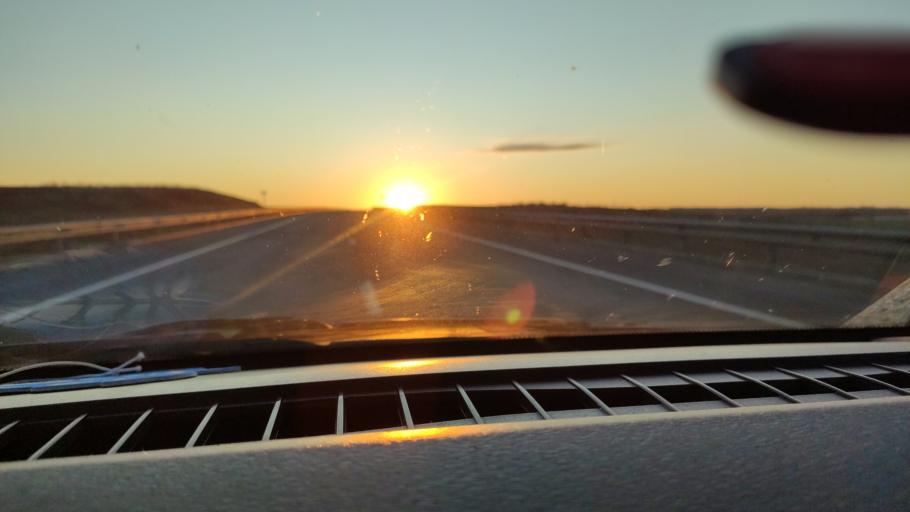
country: RU
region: Saratov
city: Yelshanka
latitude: 51.8286
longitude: 46.4001
